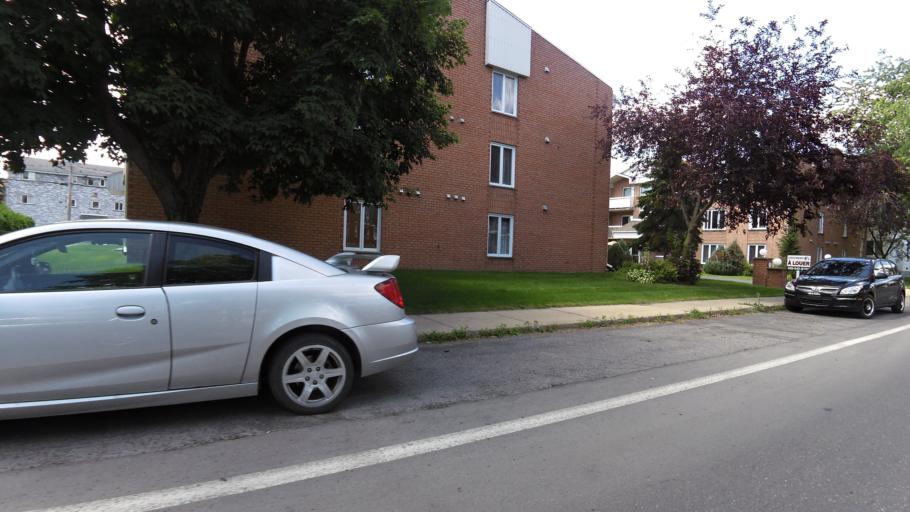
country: CA
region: Quebec
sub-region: Monteregie
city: Saint-Jean-sur-Richelieu
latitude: 45.2944
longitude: -73.2612
